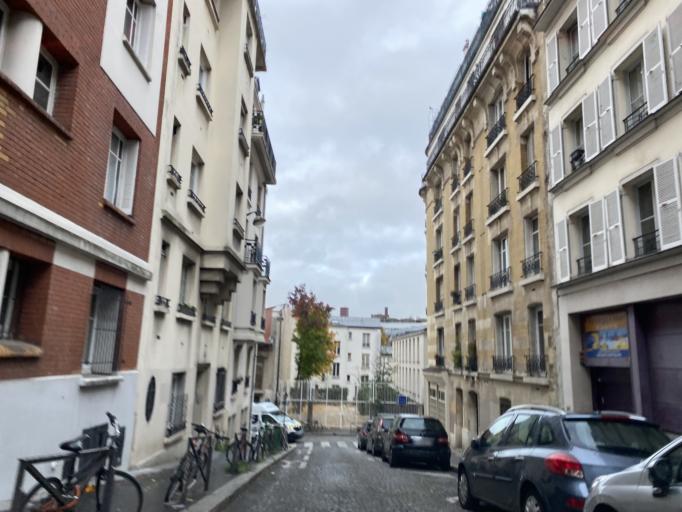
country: FR
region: Ile-de-France
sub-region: Departement de Seine-Saint-Denis
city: Le Pre-Saint-Gervais
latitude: 48.8646
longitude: 2.3926
